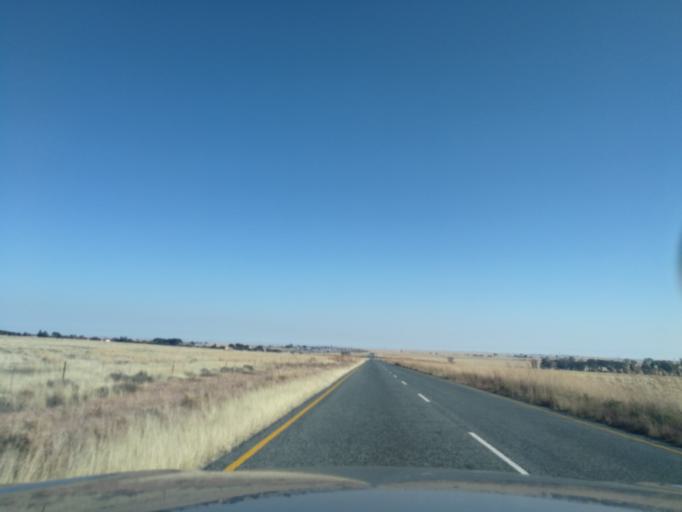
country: ZA
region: Orange Free State
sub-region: Thabo Mofutsanyana District Municipality
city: Senekal
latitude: -27.9482
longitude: 27.5807
